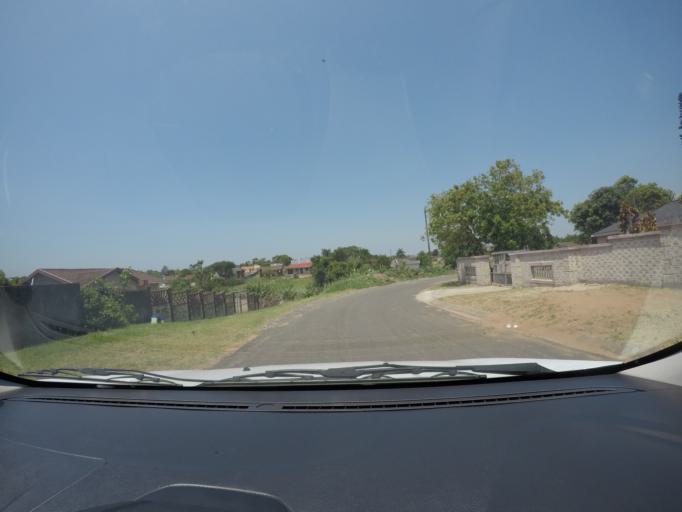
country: ZA
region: KwaZulu-Natal
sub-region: uThungulu District Municipality
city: eSikhawini
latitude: -28.8742
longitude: 31.9126
